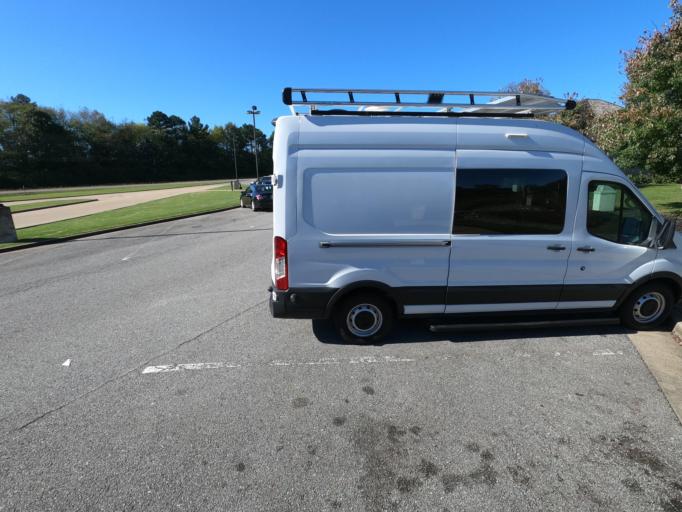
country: US
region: Alabama
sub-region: Limestone County
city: Ardmore
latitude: 35.0356
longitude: -86.8778
